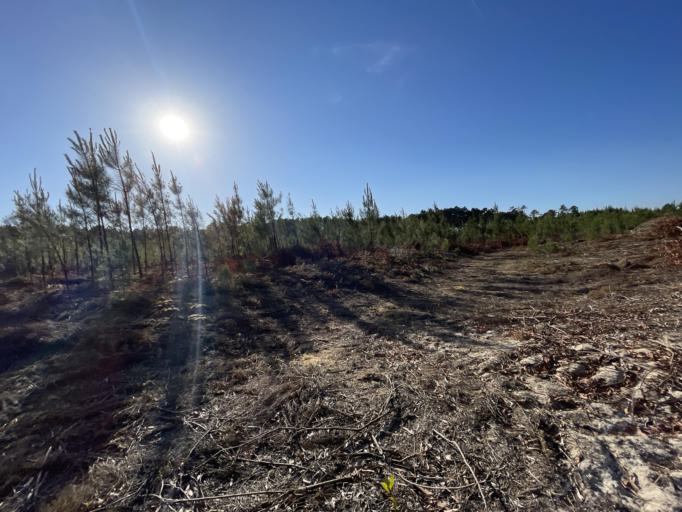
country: PT
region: Aveiro
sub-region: Ovar
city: Cortegaca
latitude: 40.9370
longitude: -8.6469
